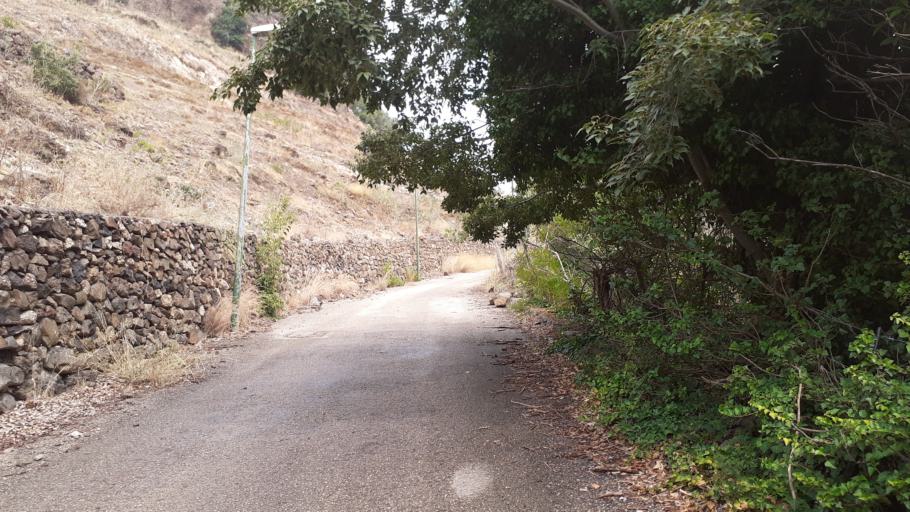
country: IT
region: Sicily
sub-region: Catania
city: Militello in Val di Catania
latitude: 37.2810
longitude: 14.8148
